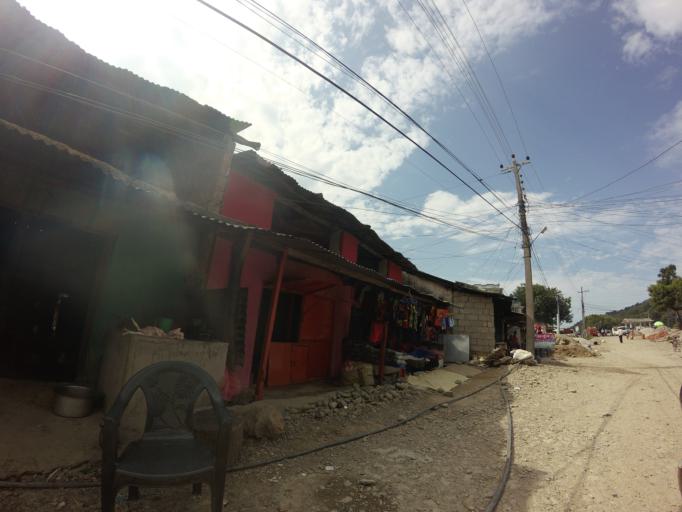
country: NP
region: Far Western
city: Tikapur
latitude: 28.6435
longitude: 81.2820
